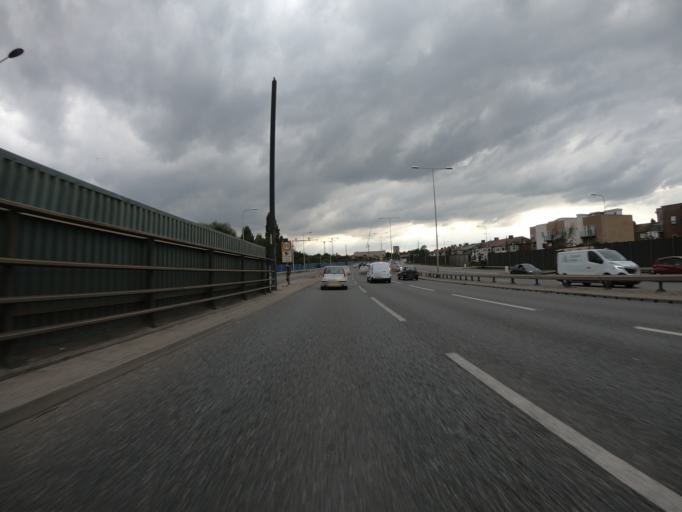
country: GB
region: England
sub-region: Greater London
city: East Ham
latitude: 51.5195
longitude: 0.0556
